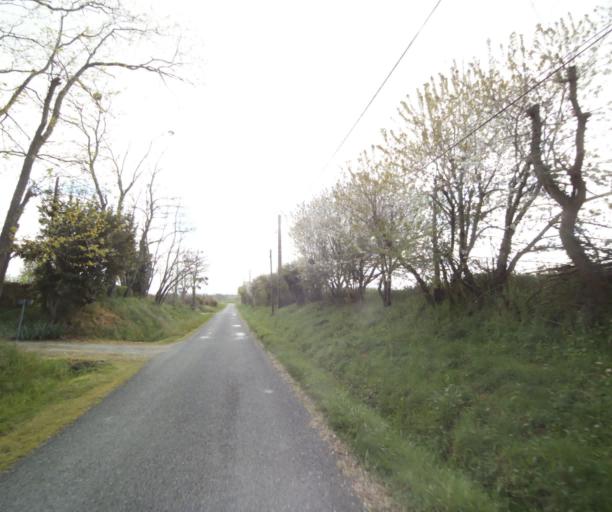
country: FR
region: Midi-Pyrenees
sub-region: Departement de l'Ariege
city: Saverdun
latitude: 43.2309
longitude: 1.5456
